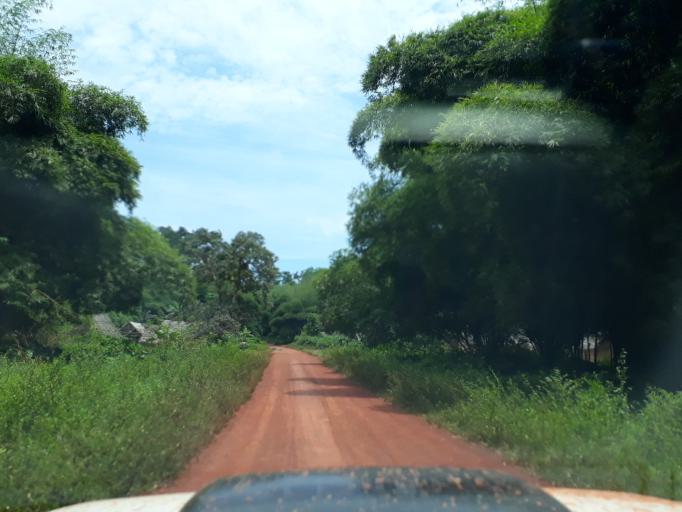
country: CD
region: Eastern Province
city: Buta
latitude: 2.5616
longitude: 24.8260
